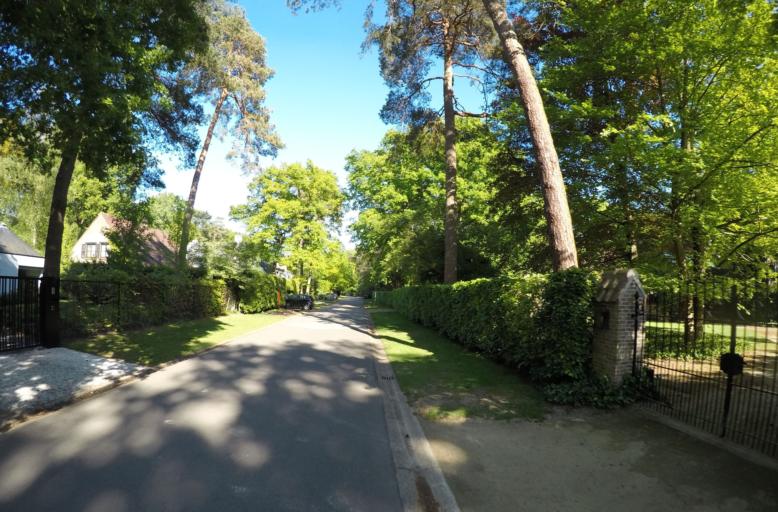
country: BE
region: Flanders
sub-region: Provincie Antwerpen
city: Schilde
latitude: 51.2527
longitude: 4.5563
